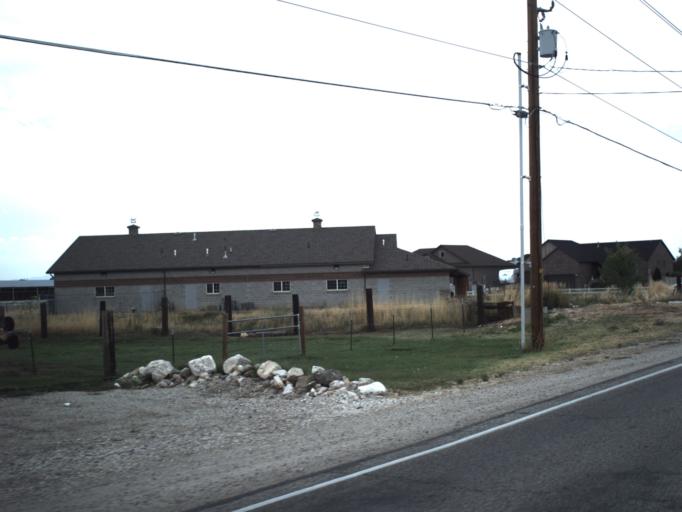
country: US
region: Utah
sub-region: Weber County
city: West Haven
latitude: 41.1965
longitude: -112.0932
